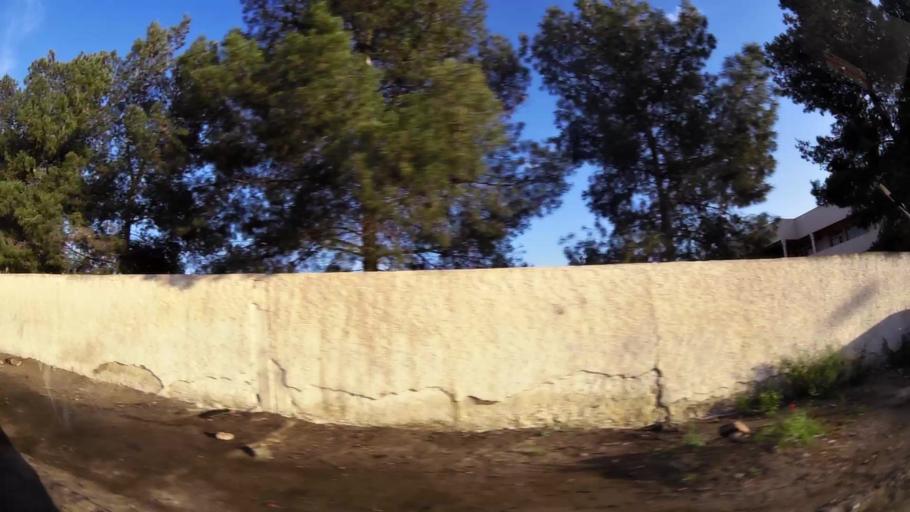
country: MA
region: Oriental
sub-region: Oujda-Angad
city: Oujda
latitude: 34.6999
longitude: -1.9179
